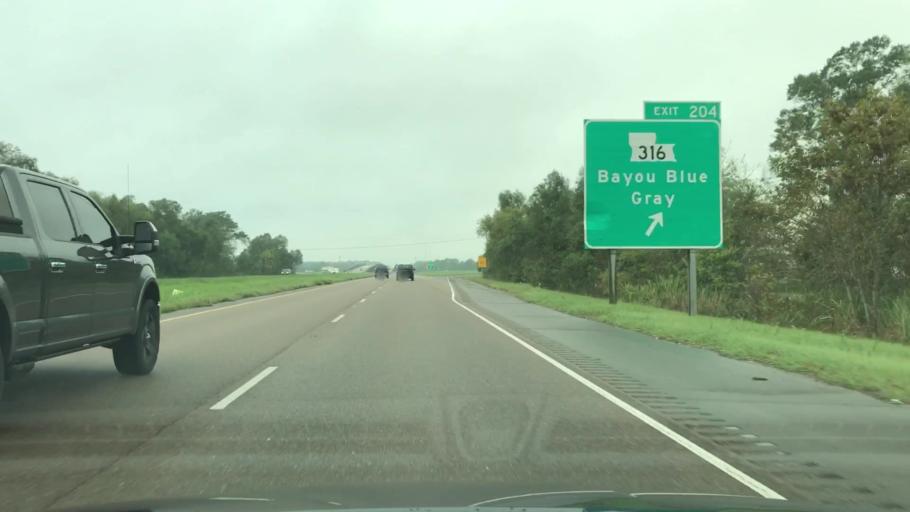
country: US
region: Louisiana
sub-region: Terrebonne Parish
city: Gray
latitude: 29.6836
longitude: -90.7422
